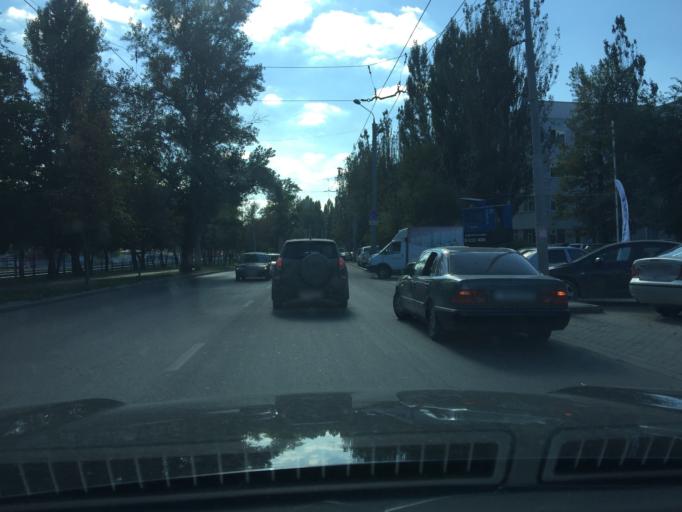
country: RU
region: Rostov
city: Imeni Chkalova
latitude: 47.2521
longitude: 39.7623
